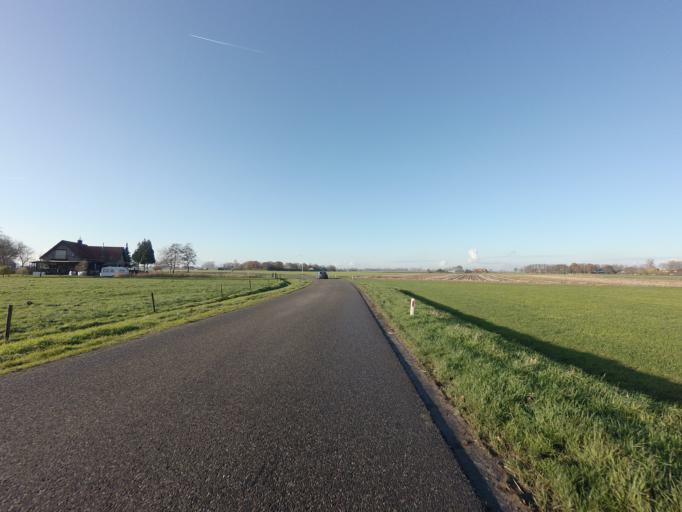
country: NL
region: Gelderland
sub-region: Gemeente Zaltbommel
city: Nederhemert-Noord
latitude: 51.7275
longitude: 5.1860
